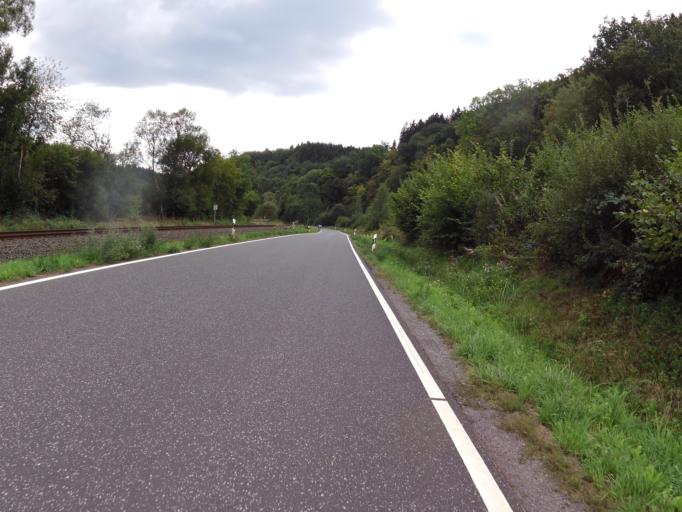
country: DE
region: Rheinland-Pfalz
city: Zendscheid
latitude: 50.0916
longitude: 6.6025
